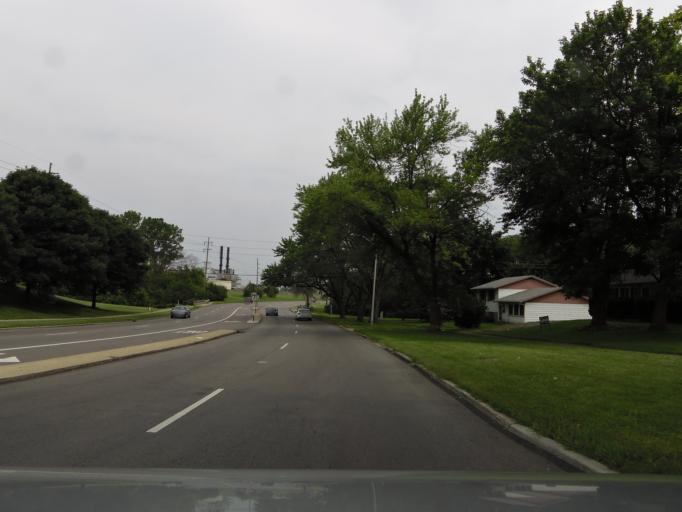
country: US
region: Ohio
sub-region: Montgomery County
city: Kettering
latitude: 39.7071
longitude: -84.1231
